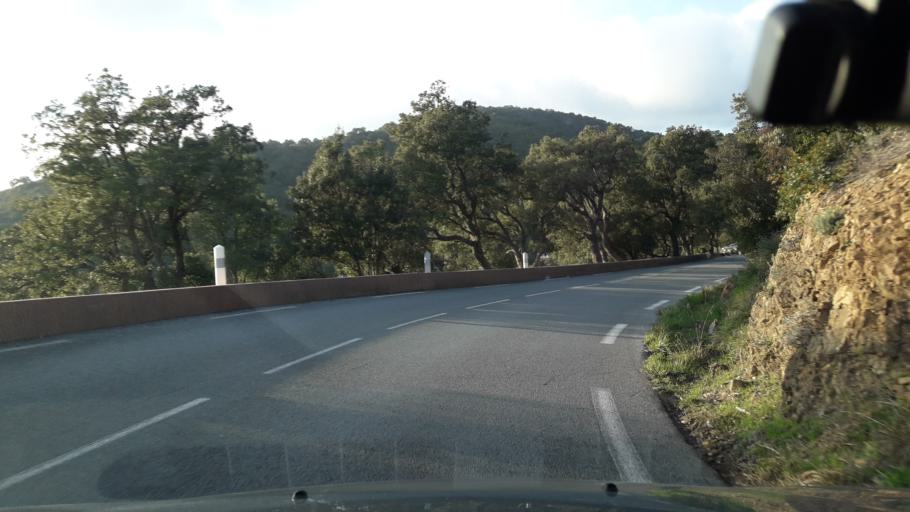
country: FR
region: Provence-Alpes-Cote d'Azur
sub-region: Departement du Var
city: Saint-Raphael
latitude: 43.5013
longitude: 6.7883
